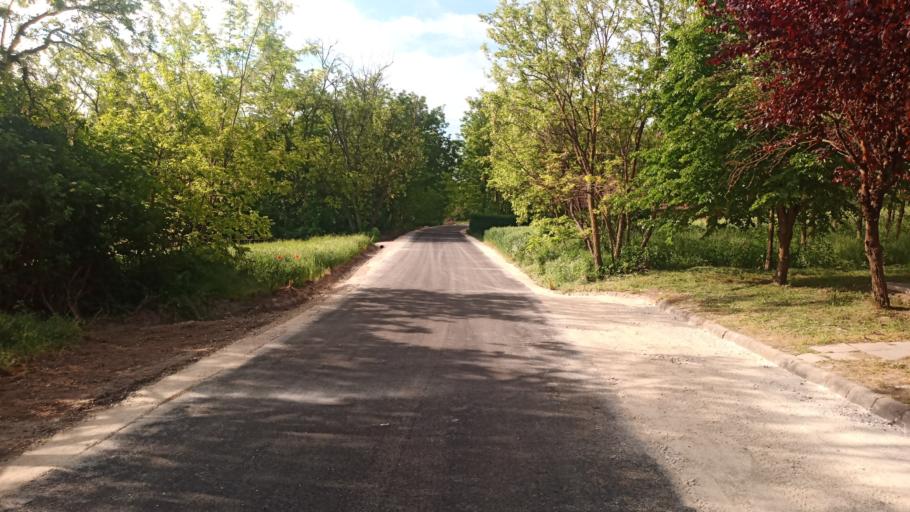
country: HU
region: Zala
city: Pacsa
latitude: 46.7001
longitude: 17.0181
